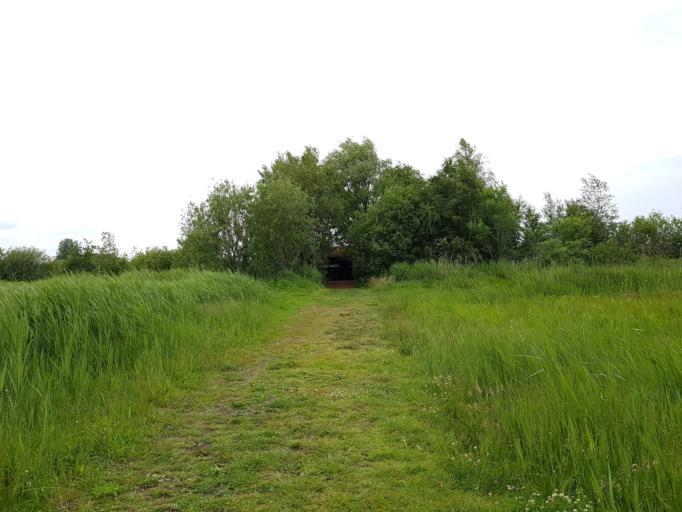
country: NL
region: Friesland
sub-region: Gemeente Tytsjerksteradiel
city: Garyp
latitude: 53.1417
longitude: 5.9396
